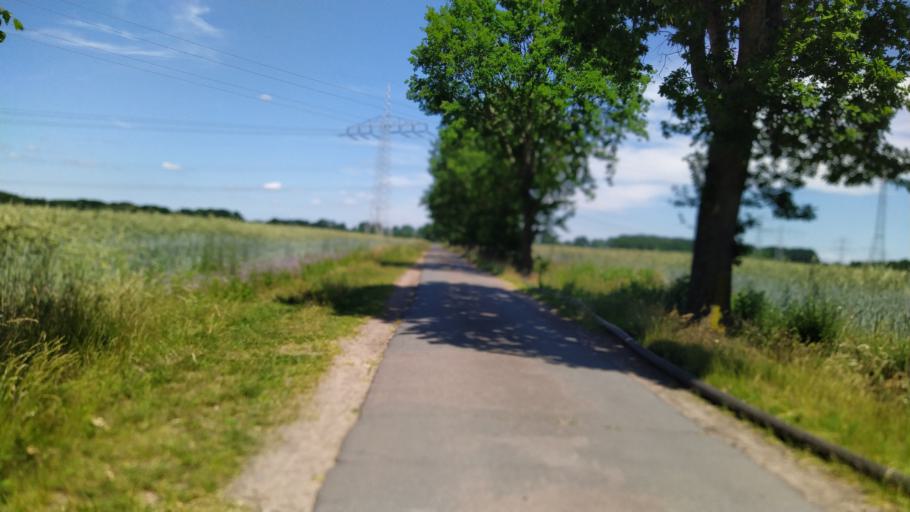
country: DE
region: Lower Saxony
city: Deinste
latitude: 53.5088
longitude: 9.4404
